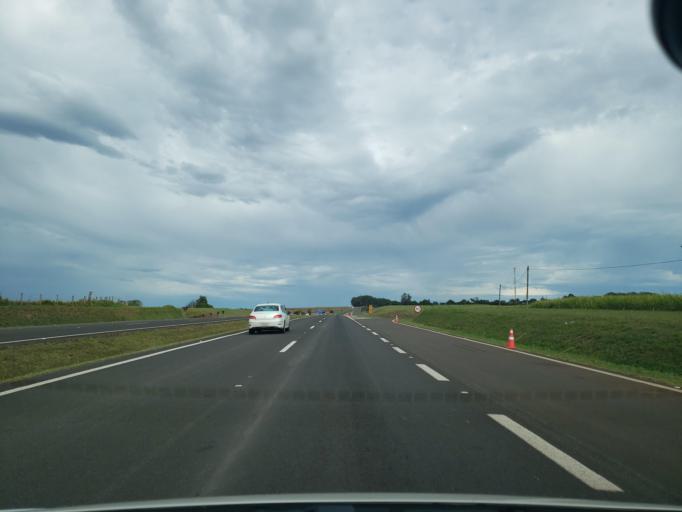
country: BR
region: Sao Paulo
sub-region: Dois Corregos
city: Dois Corregos
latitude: -22.2636
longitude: -48.3786
